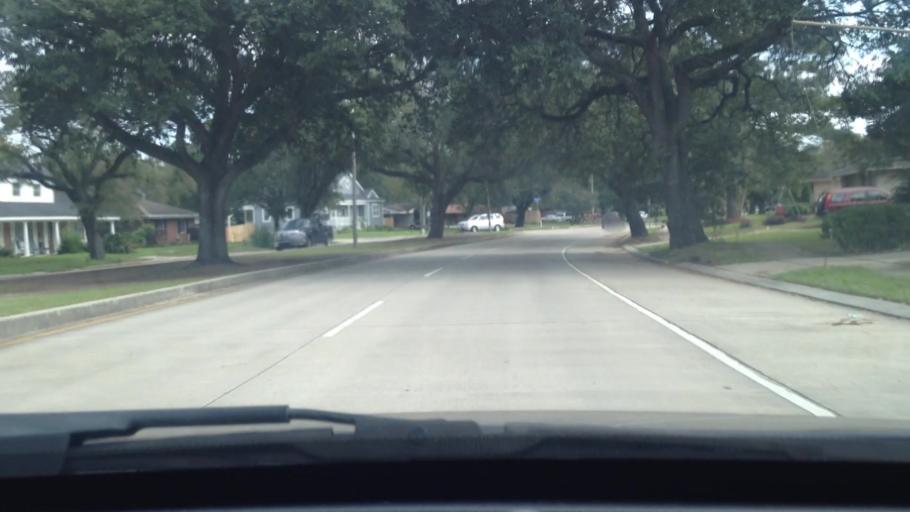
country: US
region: Louisiana
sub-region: Saint Bernard Parish
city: Arabi
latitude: 29.9235
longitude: -90.0026
